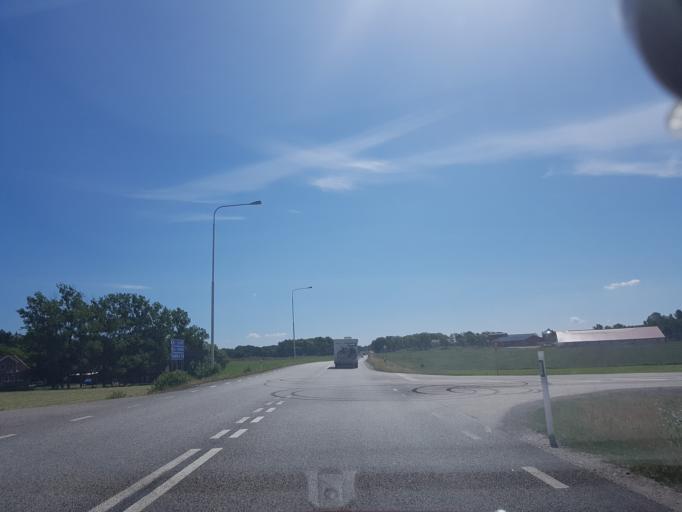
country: SE
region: Vaestra Goetaland
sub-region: Orust
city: Henan
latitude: 58.1496
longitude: 11.5888
